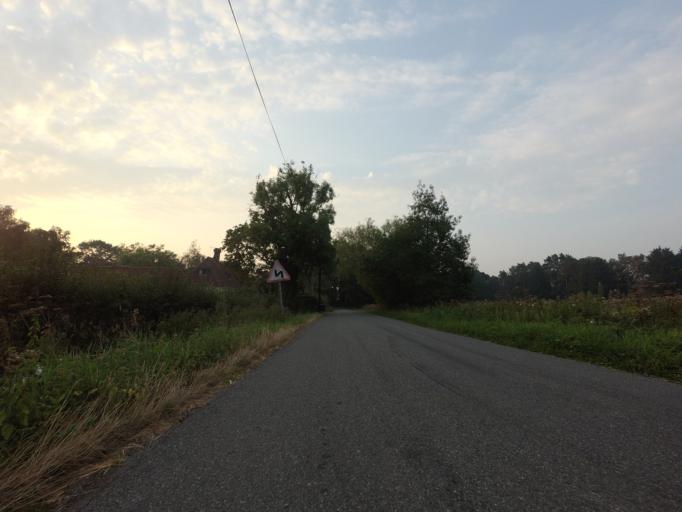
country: GB
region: England
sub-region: Kent
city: Lenham
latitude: 51.1834
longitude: 0.7184
